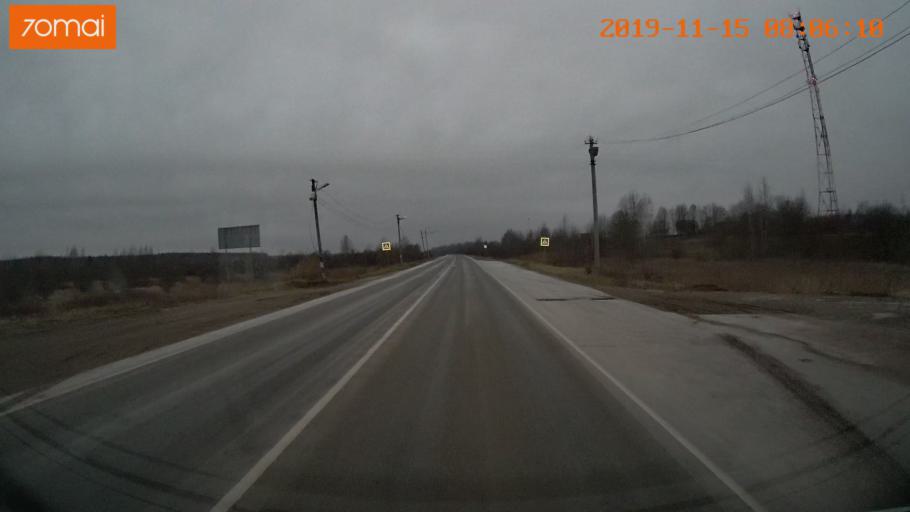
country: RU
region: Vologda
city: Cherepovets
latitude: 59.0209
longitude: 38.0438
